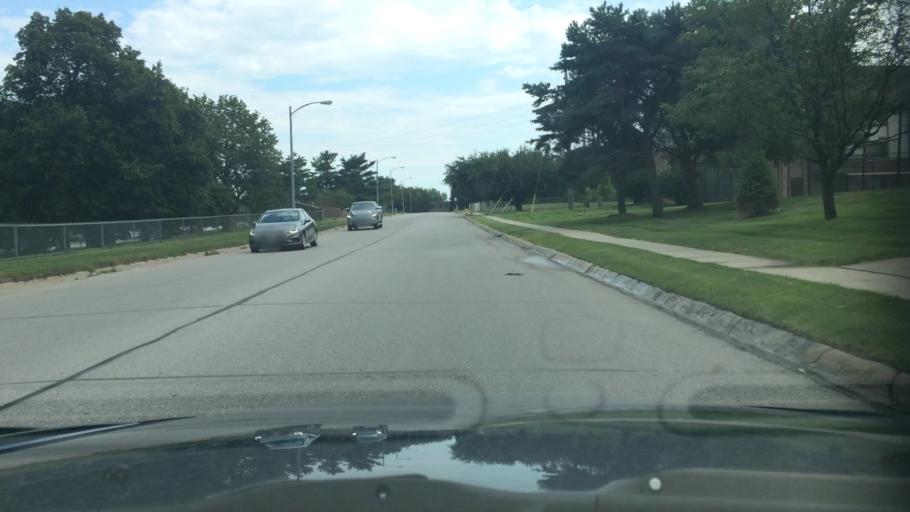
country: US
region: Nebraska
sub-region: Douglas County
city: Ralston
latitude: 41.1985
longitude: -96.0691
